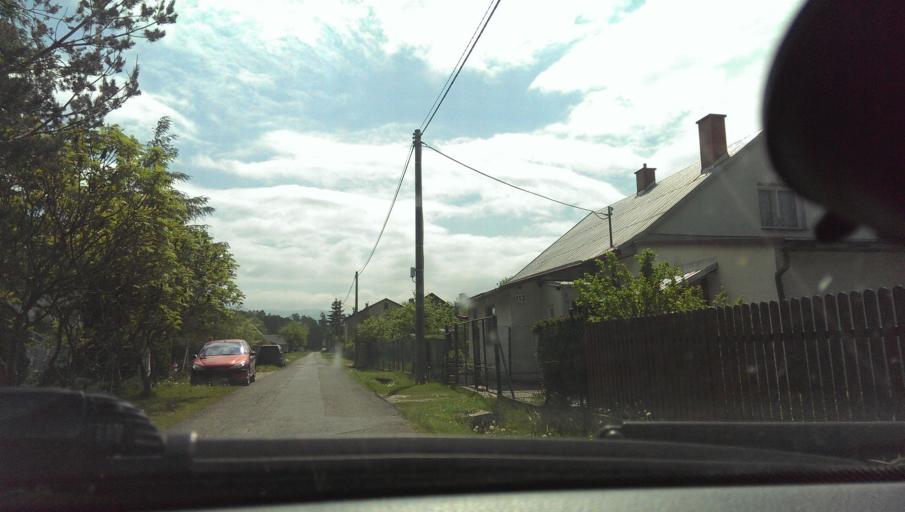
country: CZ
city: Lichnov (o. Novy Jicin)
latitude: 49.5687
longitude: 18.1831
